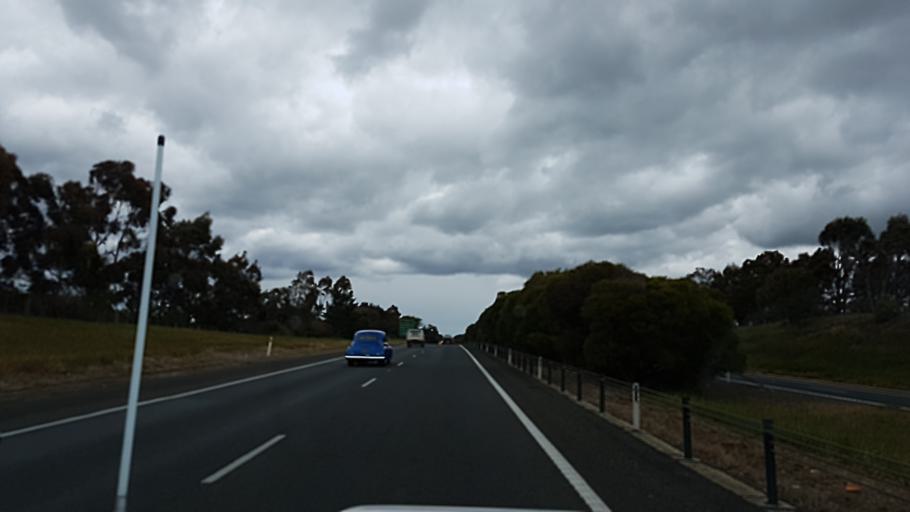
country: AU
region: Victoria
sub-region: Moorabool
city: Bacchus Marsh
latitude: -37.6116
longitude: 144.3037
